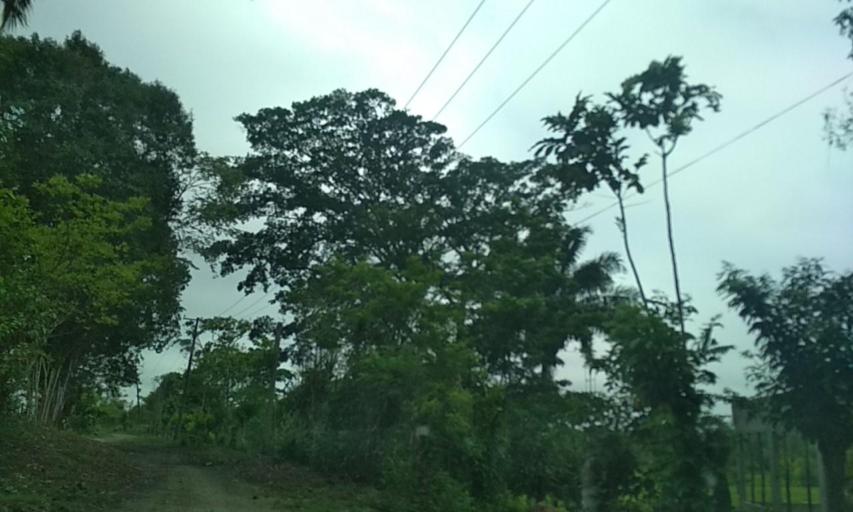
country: MX
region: Veracruz
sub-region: Uxpanapa
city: Poblado 10
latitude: 17.5041
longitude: -94.1620
